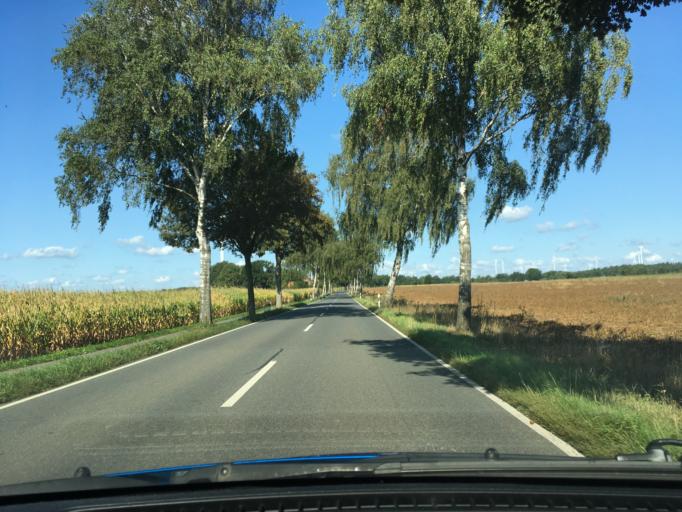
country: DE
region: Lower Saxony
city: Hermannsburg
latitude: 52.8511
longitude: 10.0656
